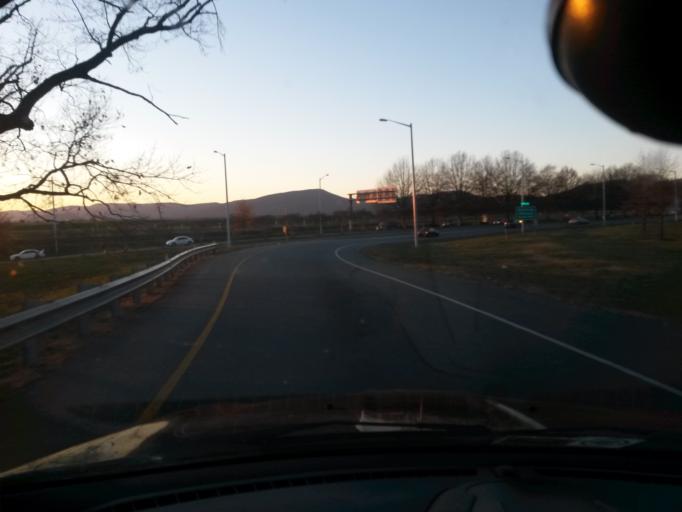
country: US
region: Virginia
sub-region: Roanoke County
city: Hollins
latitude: 37.3155
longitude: -79.9663
